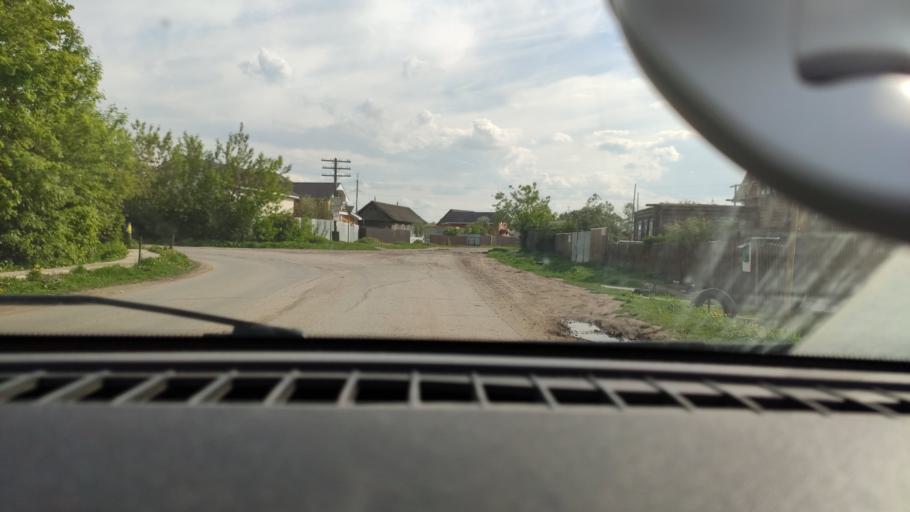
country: RU
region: Perm
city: Kultayevo
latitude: 57.9251
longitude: 56.0095
